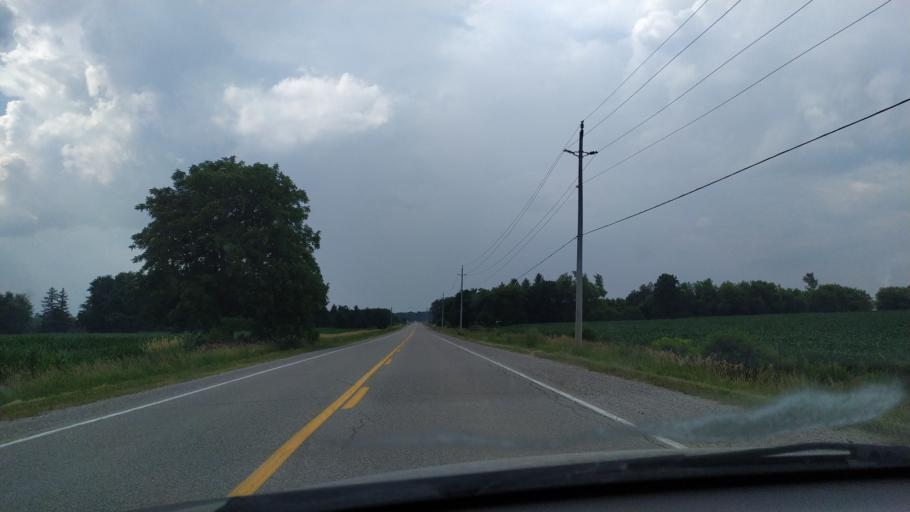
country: CA
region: Ontario
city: London
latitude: 43.2139
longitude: -81.1596
